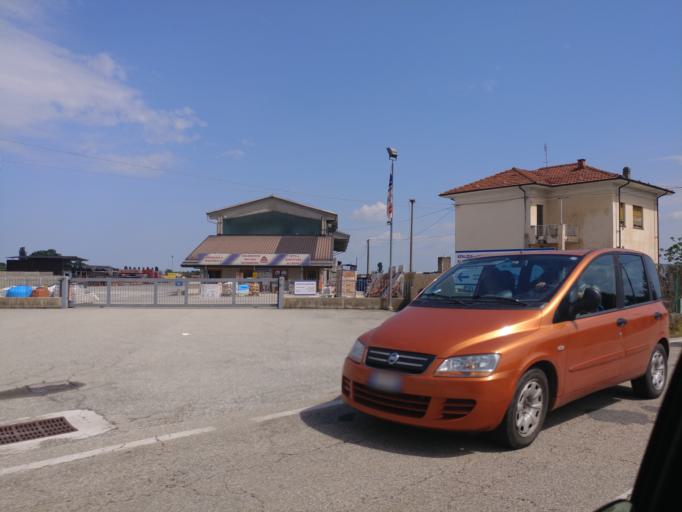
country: IT
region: Piedmont
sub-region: Provincia di Torino
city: Cavour
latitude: 44.7773
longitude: 7.3862
